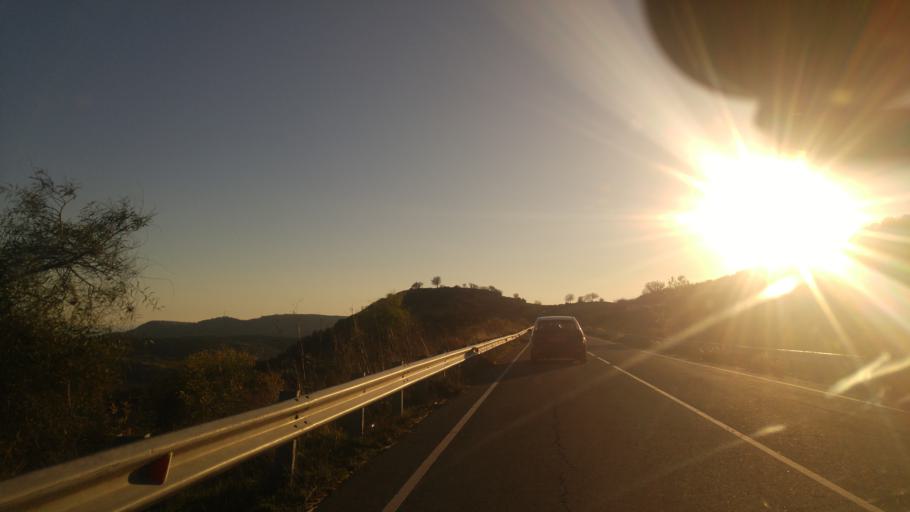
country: CY
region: Limassol
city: Pachna
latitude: 34.8311
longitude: 32.8062
